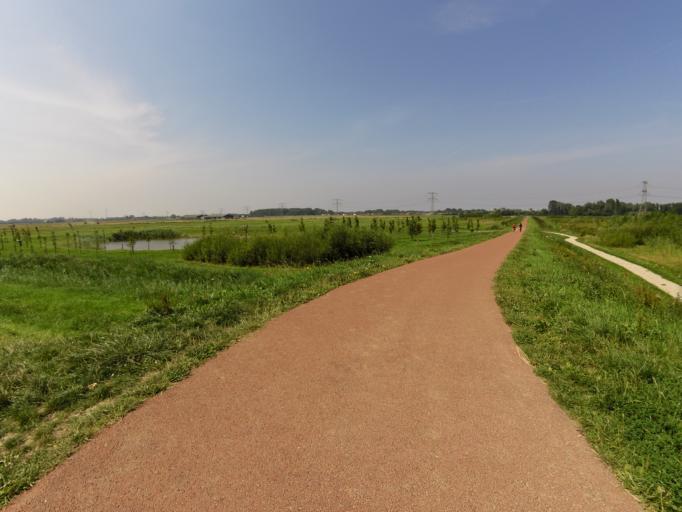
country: NL
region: South Holland
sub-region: Gemeente Dordrecht
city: Dordrecht
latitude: 51.7632
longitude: 4.6841
